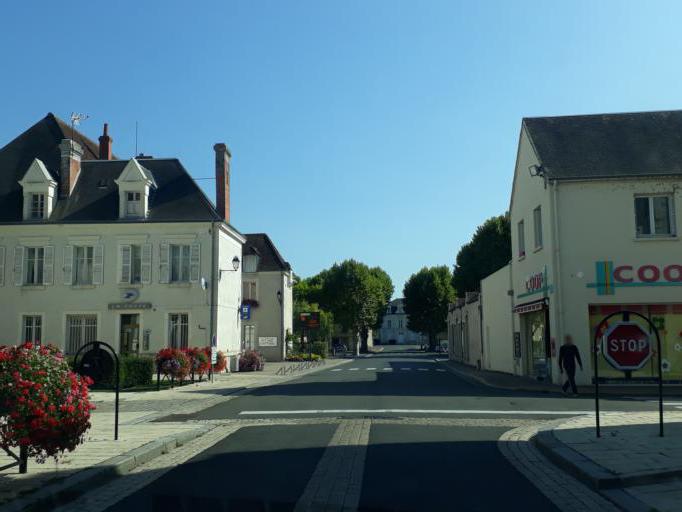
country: FR
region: Centre
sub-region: Departement du Loir-et-Cher
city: Selles-sur-Cher
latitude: 47.2752
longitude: 1.5535
